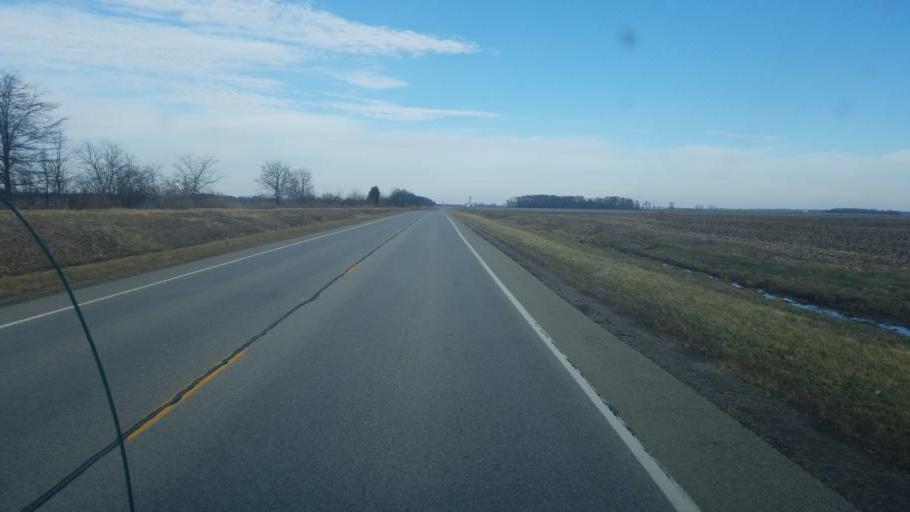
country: US
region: Illinois
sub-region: White County
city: Carmi
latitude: 38.1260
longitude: -88.1047
